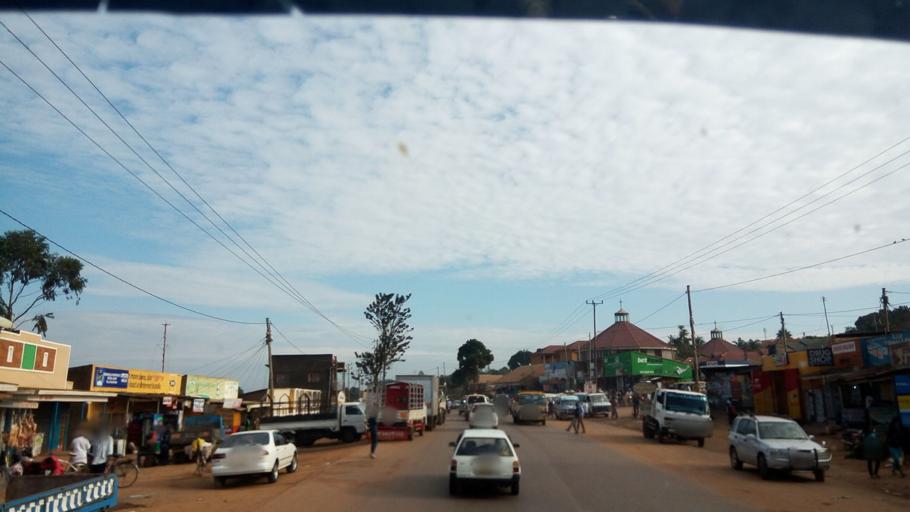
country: UG
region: Central Region
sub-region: Wakiso District
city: Wakiso
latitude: 0.4590
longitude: 32.5290
